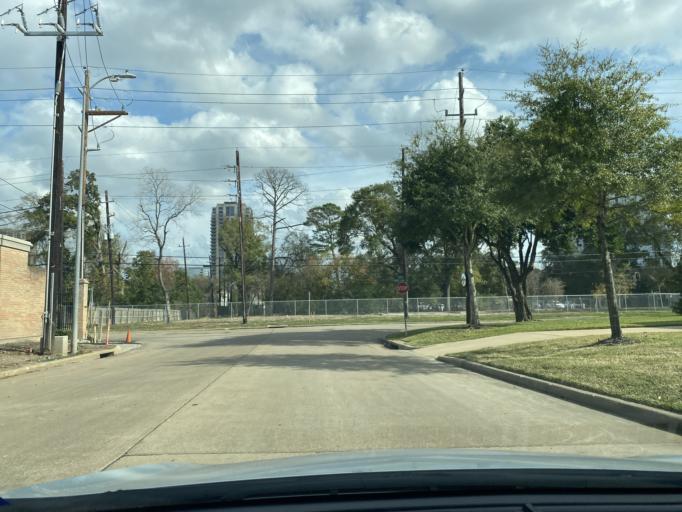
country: US
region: Texas
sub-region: Harris County
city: Hunters Creek Village
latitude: 29.7558
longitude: -95.4635
